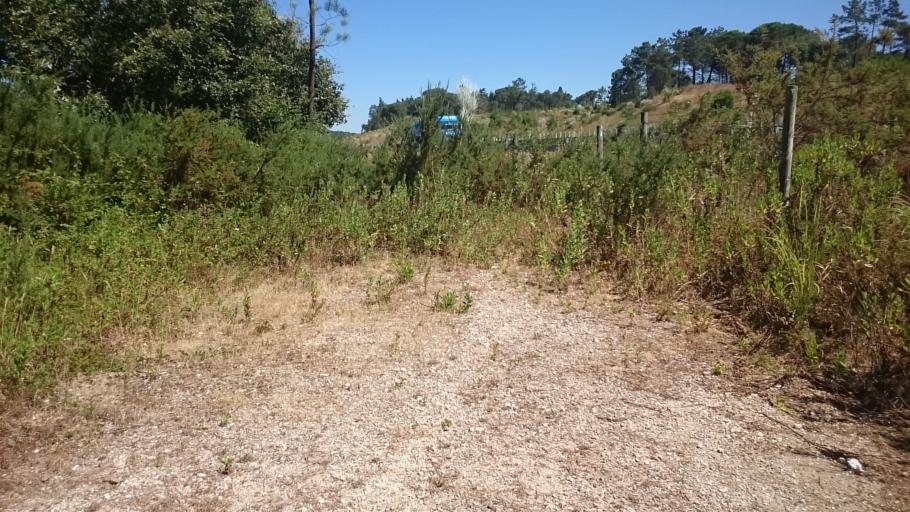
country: PT
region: Leiria
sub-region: Leiria
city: Souto da Carpalhosa
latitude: 39.8339
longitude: -8.8347
